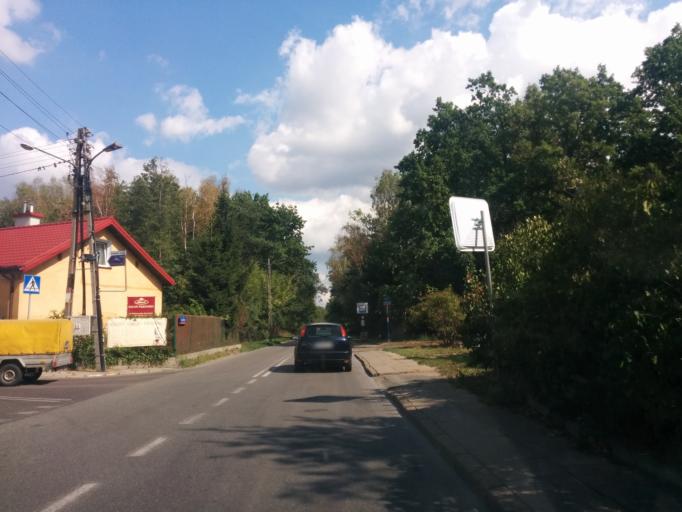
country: PL
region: Masovian Voivodeship
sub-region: Warszawa
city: Bialoleka
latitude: 52.3375
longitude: 20.9652
